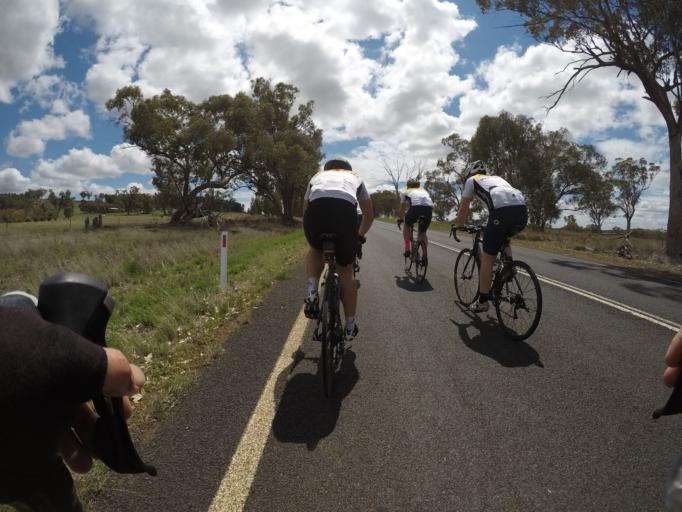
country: AU
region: New South Wales
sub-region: Dubbo Municipality
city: Dubbo
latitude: -32.4454
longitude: 148.5835
